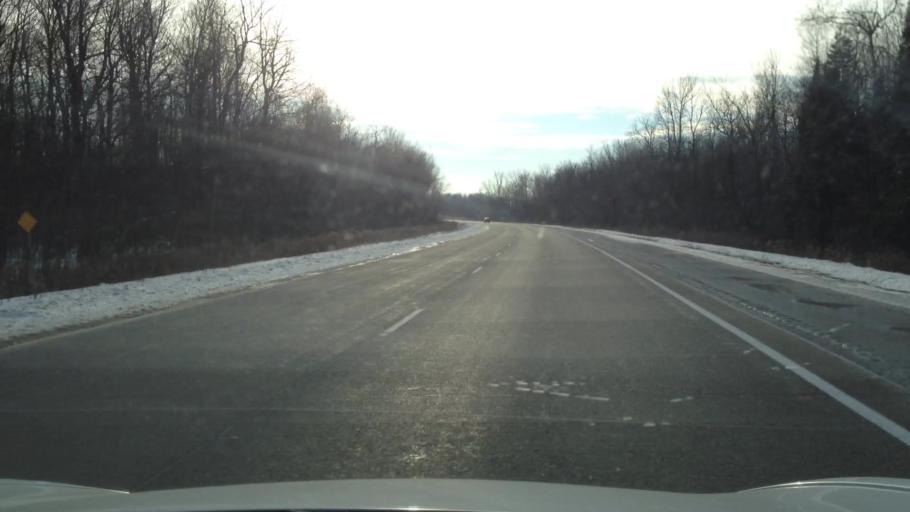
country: CA
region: Ontario
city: Hawkesbury
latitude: 45.4443
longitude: -74.7310
